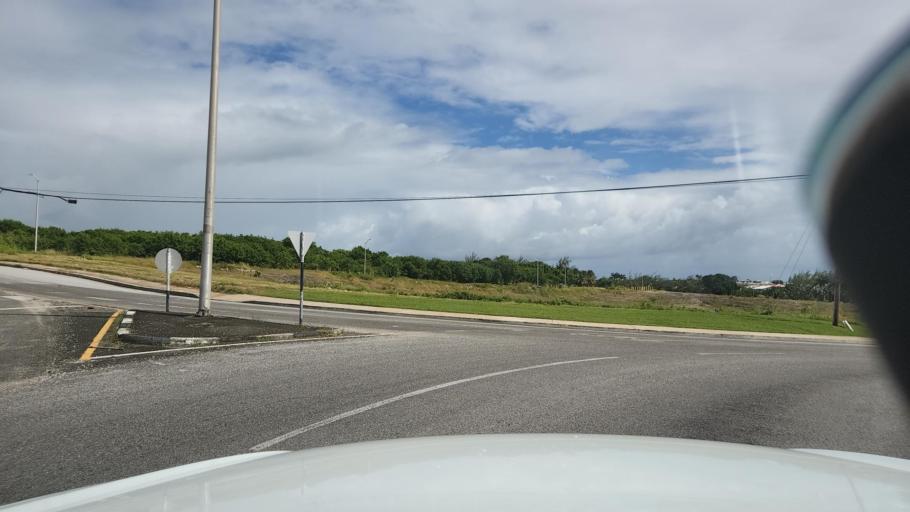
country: BB
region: Christ Church
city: Oistins
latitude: 13.0805
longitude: -59.5305
